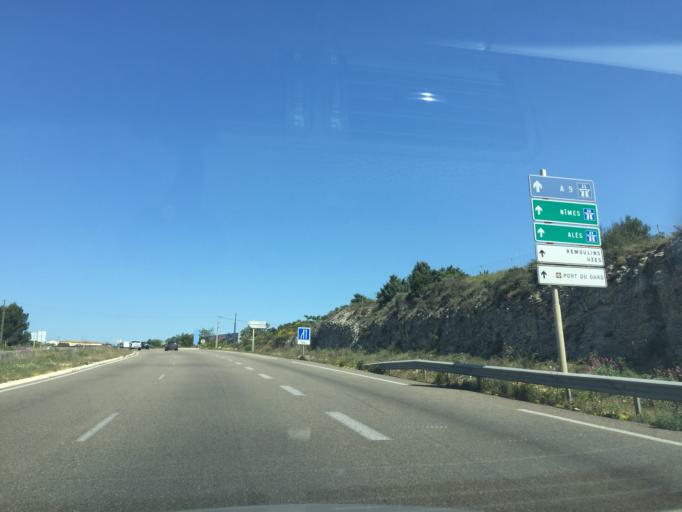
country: FR
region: Languedoc-Roussillon
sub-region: Departement du Gard
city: Les Angles
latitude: 43.9554
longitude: 4.7560
